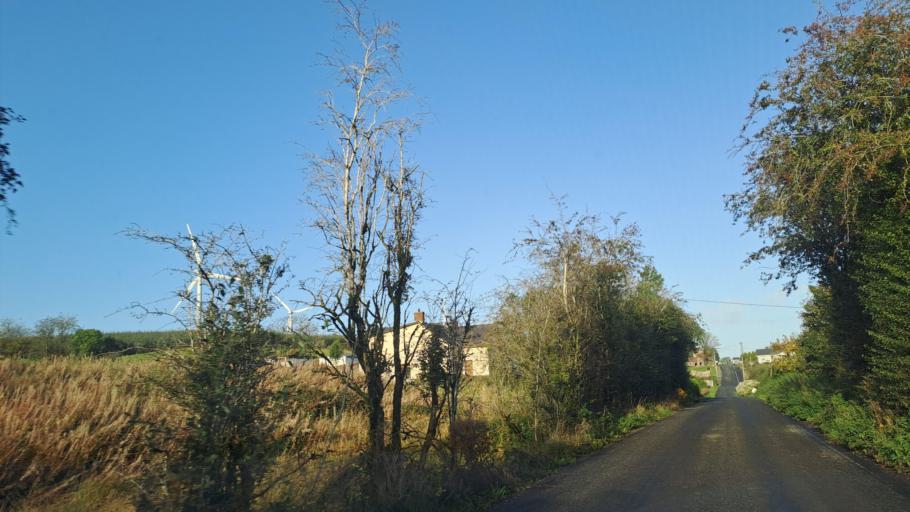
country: IE
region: Ulster
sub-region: County Monaghan
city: Castleblayney
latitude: 54.0840
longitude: -6.8570
